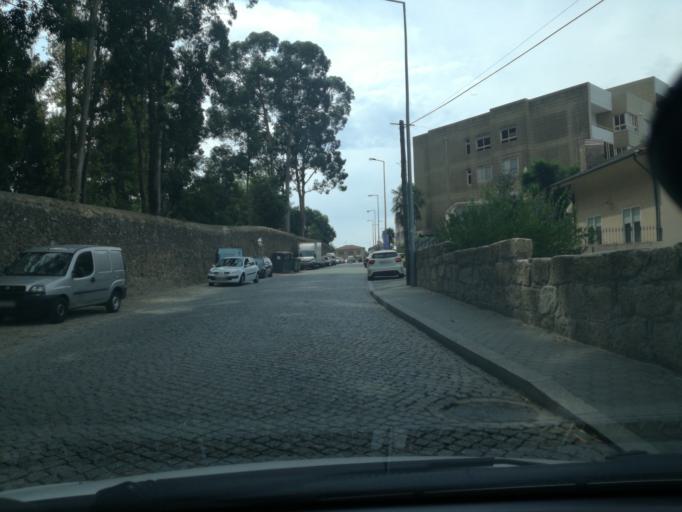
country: PT
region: Porto
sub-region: Vila Nova de Gaia
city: Grijo
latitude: 41.0305
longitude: -8.5890
